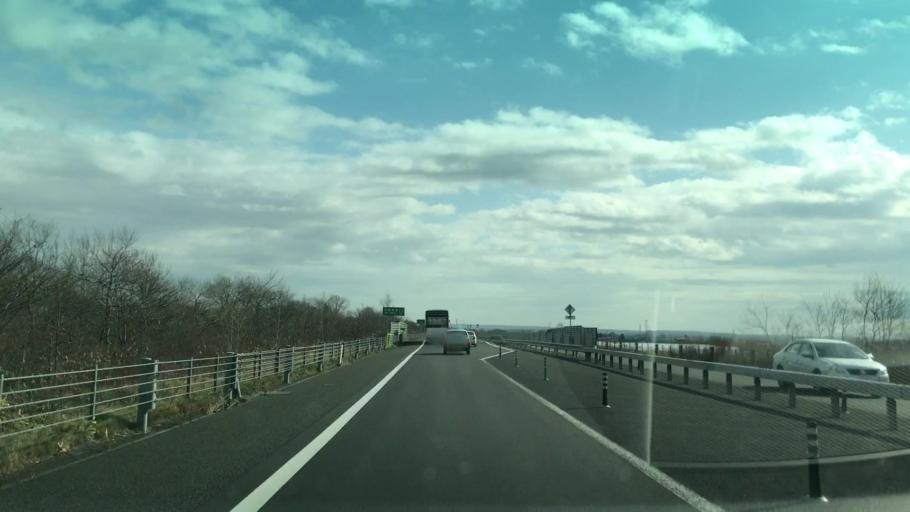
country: JP
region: Hokkaido
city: Tomakomai
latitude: 42.5931
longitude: 141.9136
